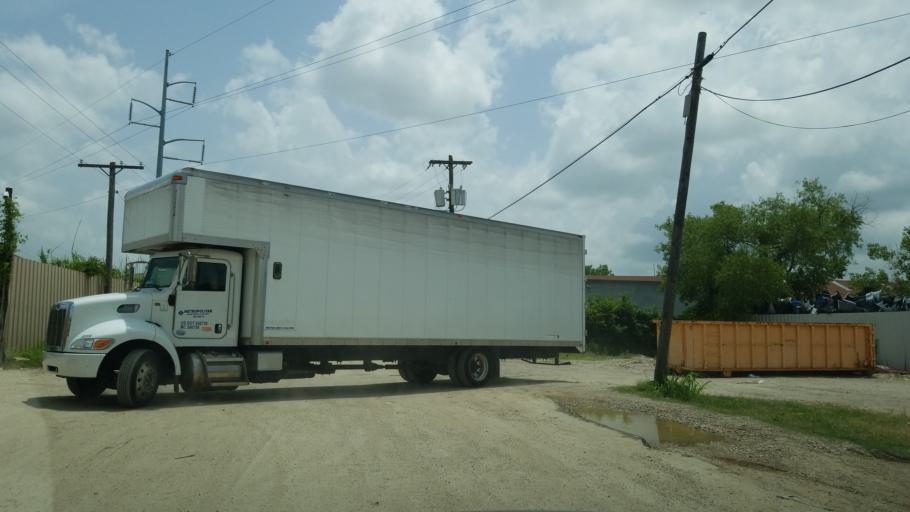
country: US
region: Texas
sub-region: Dallas County
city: Cockrell Hill
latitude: 32.7830
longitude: -96.8919
